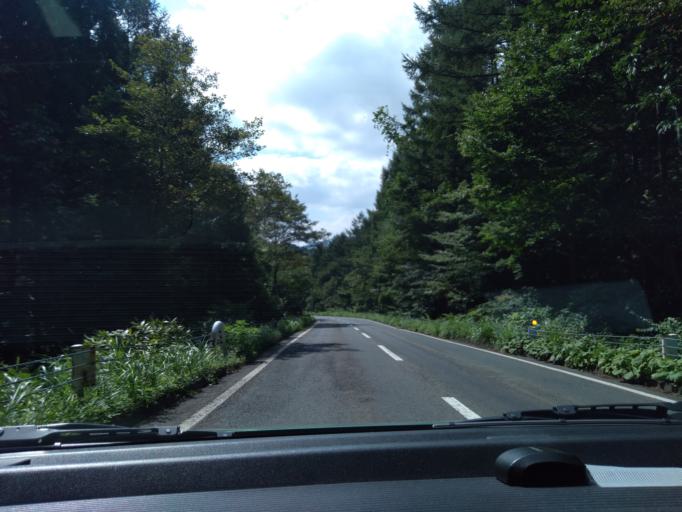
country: JP
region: Iwate
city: Shizukuishi
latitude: 39.6398
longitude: 141.0129
